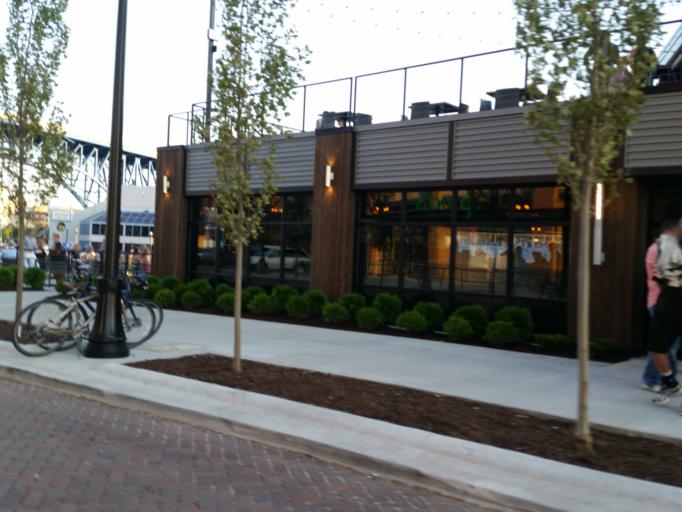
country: US
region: Ohio
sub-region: Cuyahoga County
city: Cleveland
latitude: 41.4997
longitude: -81.7067
